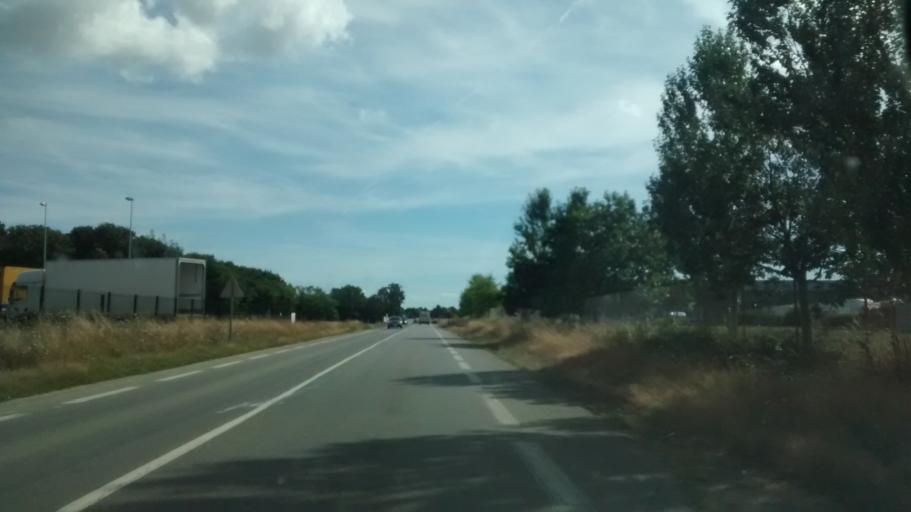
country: FR
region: Pays de la Loire
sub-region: Departement de la Loire-Atlantique
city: Pont-Saint-Martin
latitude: 47.1518
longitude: -1.6003
